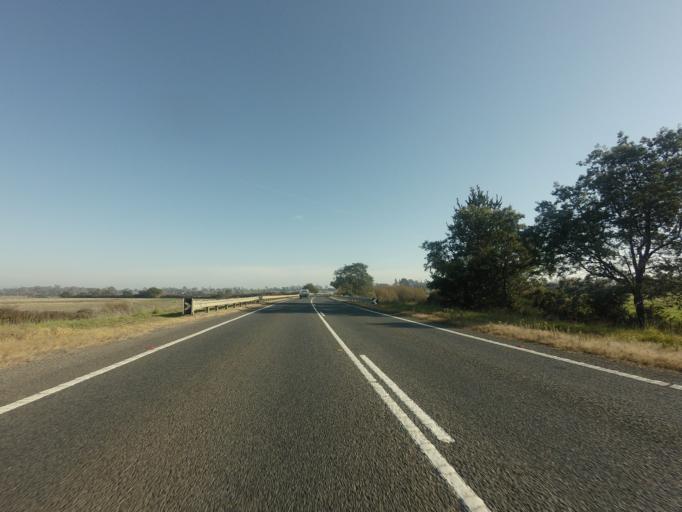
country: AU
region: Tasmania
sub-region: Northern Midlands
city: Longford
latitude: -41.5813
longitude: 147.1081
